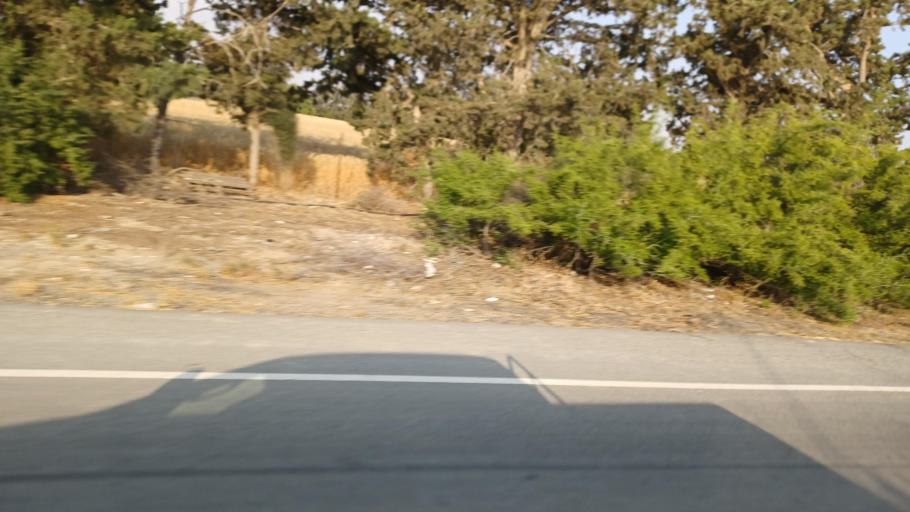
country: CY
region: Larnaka
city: Tersefanou
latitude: 34.8250
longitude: 33.5137
